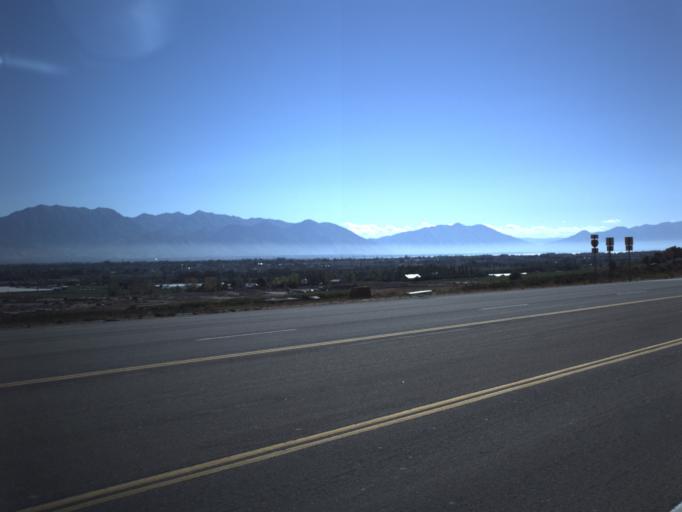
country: US
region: Utah
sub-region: Utah County
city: Saratoga Springs
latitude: 40.4117
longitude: -111.9229
